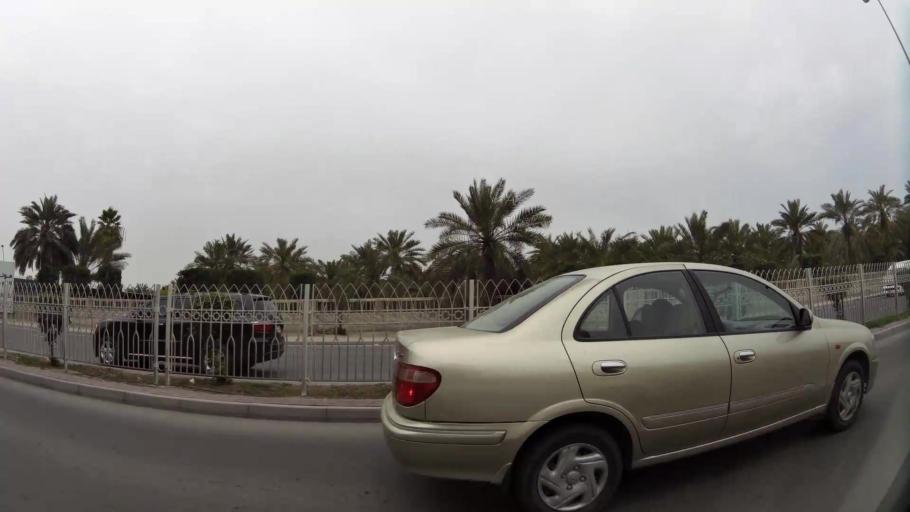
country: BH
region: Manama
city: Jidd Hafs
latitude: 26.2205
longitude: 50.5634
